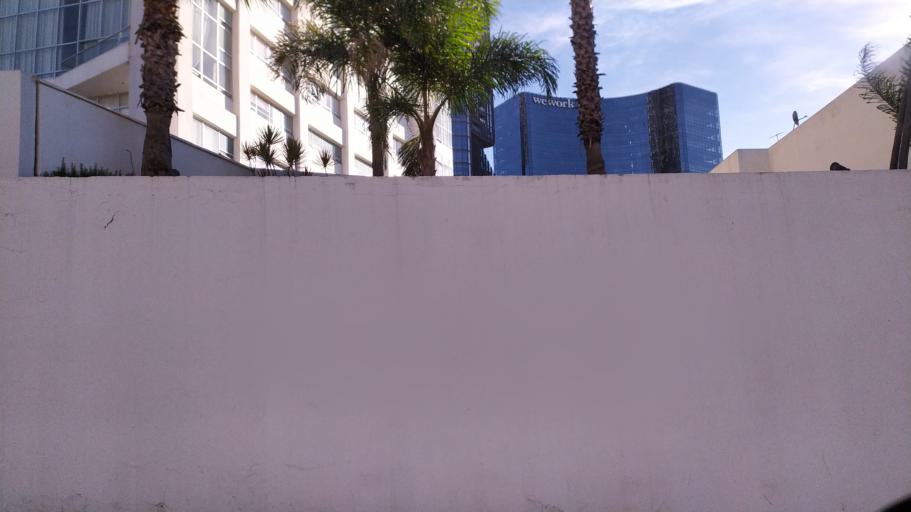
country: MX
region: Jalisco
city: Zapopan2
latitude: 20.7061
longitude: -103.4142
